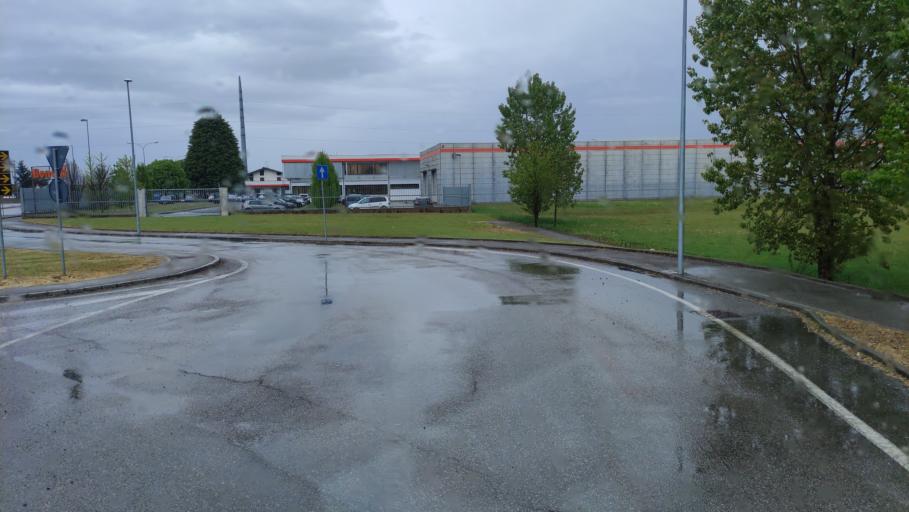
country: IT
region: Lombardy
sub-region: Provincia di Brescia
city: Rudiano
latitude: 45.5001
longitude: 9.8800
